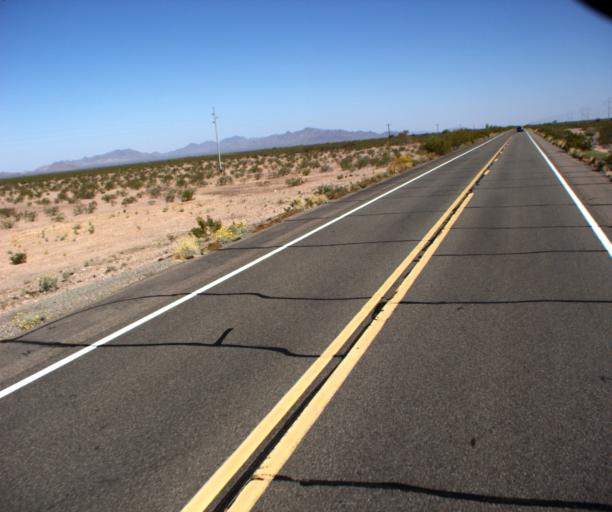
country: US
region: Arizona
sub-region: La Paz County
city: Quartzsite
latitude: 33.3426
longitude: -114.2170
